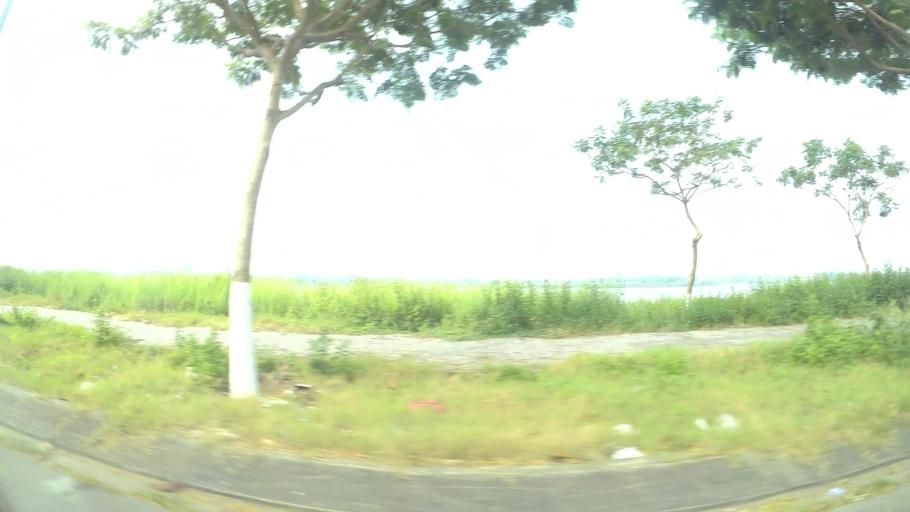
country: VN
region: Da Nang
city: Son Tra
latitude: 16.0460
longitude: 108.2352
